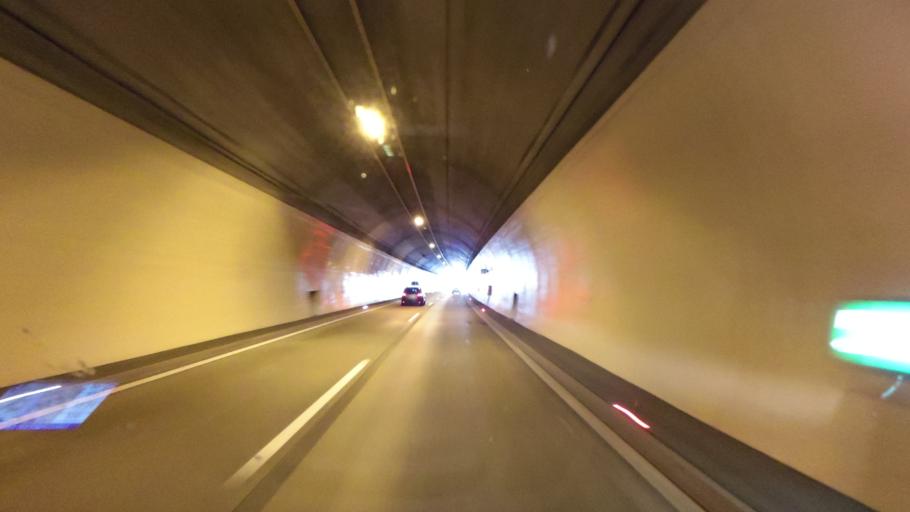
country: AT
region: Carinthia
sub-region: Politischer Bezirk Villach Land
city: Fresach
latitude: 46.6631
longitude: 13.7215
